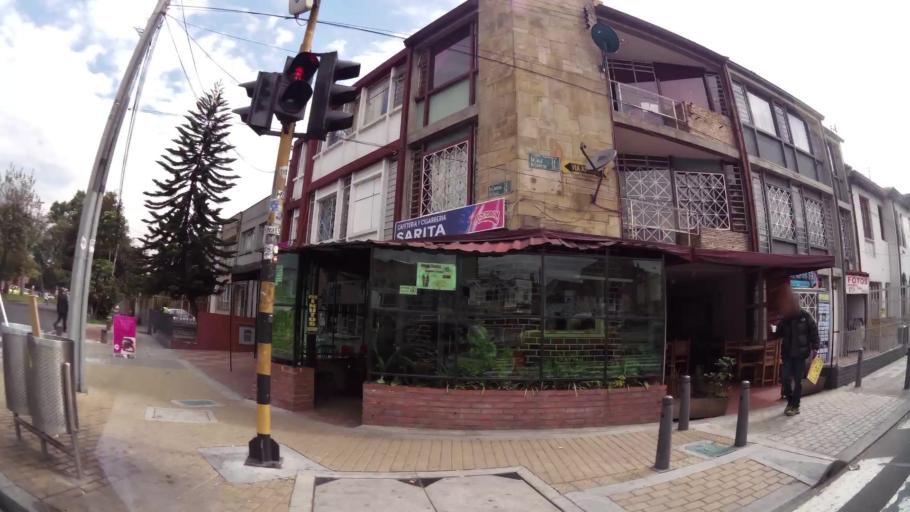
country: CO
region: Bogota D.C.
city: Bogota
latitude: 4.6242
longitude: -74.0762
